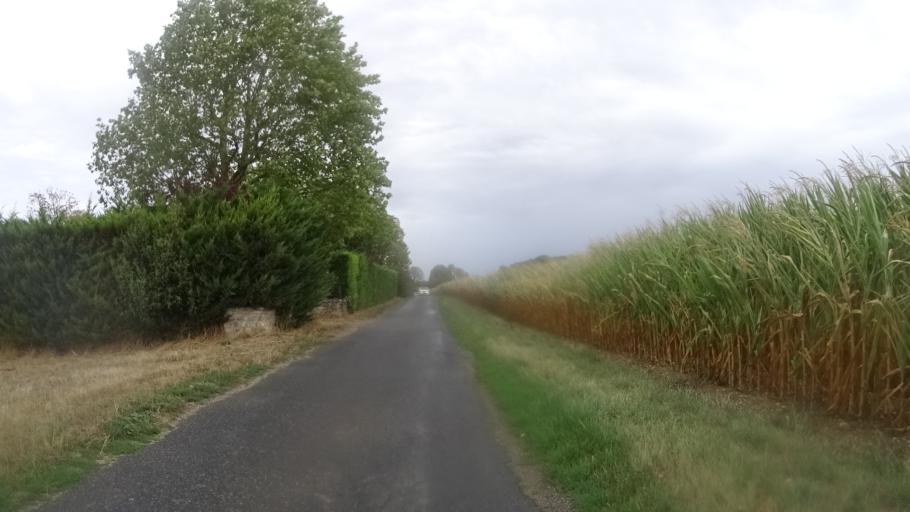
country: FR
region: Centre
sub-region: Departement du Loiret
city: Boynes
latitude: 48.1819
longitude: 2.3780
